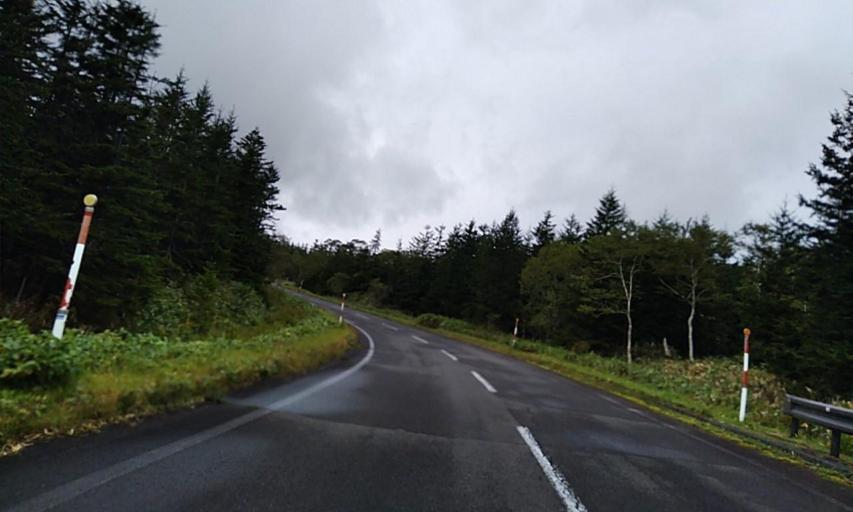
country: JP
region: Hokkaido
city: Abashiri
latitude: 43.6069
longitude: 144.5882
